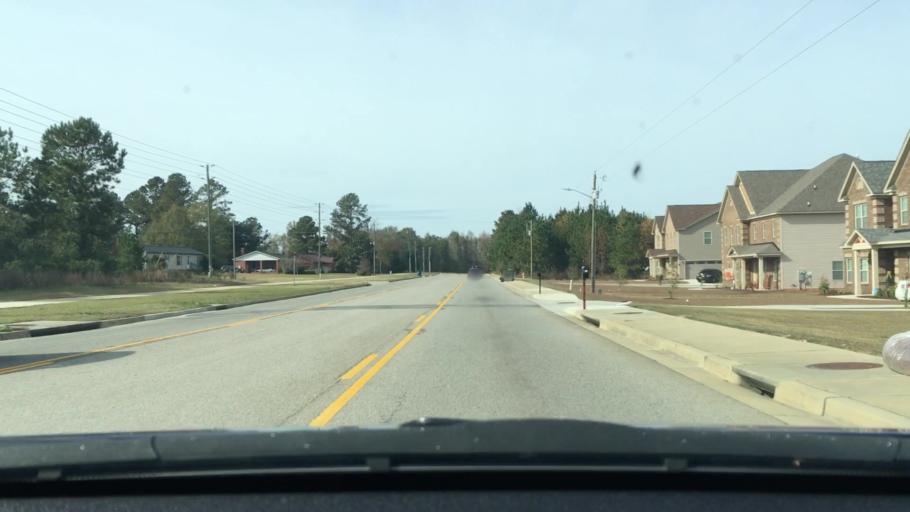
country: US
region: South Carolina
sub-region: Sumter County
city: Cane Savannah
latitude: 33.9321
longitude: -80.4150
